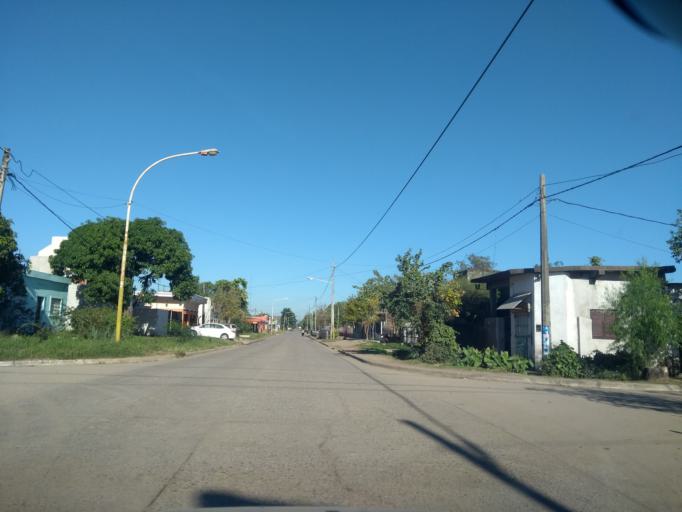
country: AR
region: Chaco
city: Barranqueras
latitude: -27.4842
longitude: -58.9288
